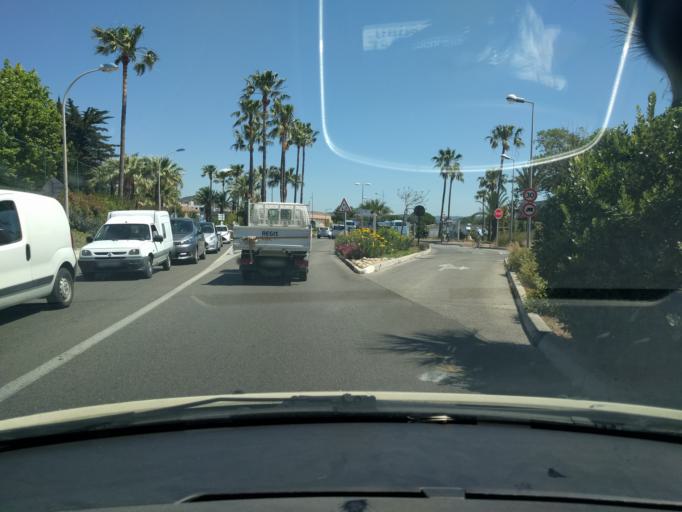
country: FR
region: Provence-Alpes-Cote d'Azur
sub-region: Departement du Var
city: Hyeres
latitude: 43.1055
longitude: 6.1280
